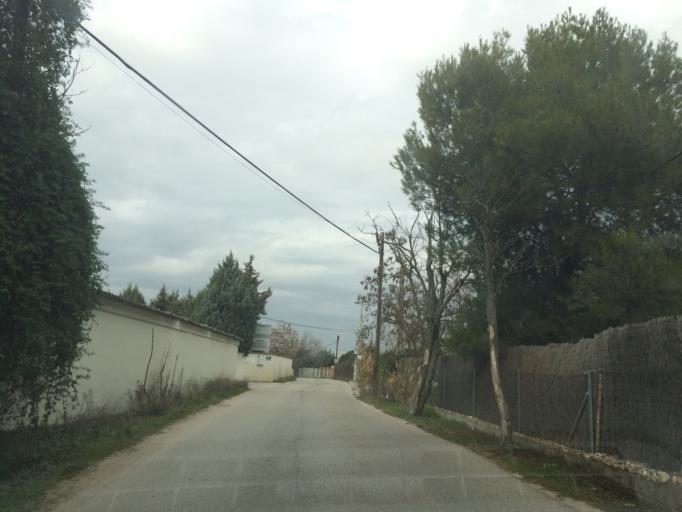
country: ES
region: Madrid
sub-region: Provincia de Madrid
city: Arroyomolinos
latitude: 40.3032
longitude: -3.9449
